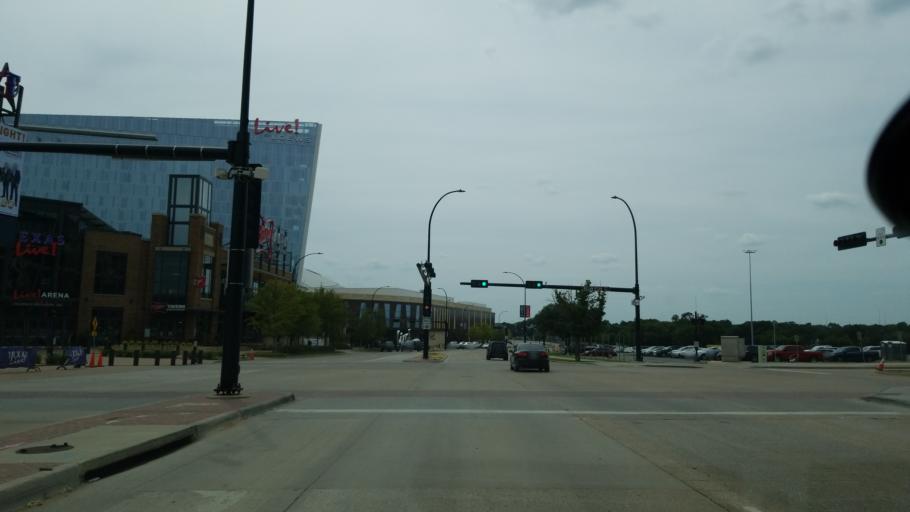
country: US
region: Texas
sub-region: Tarrant County
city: Arlington
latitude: 32.7500
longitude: -97.0839
